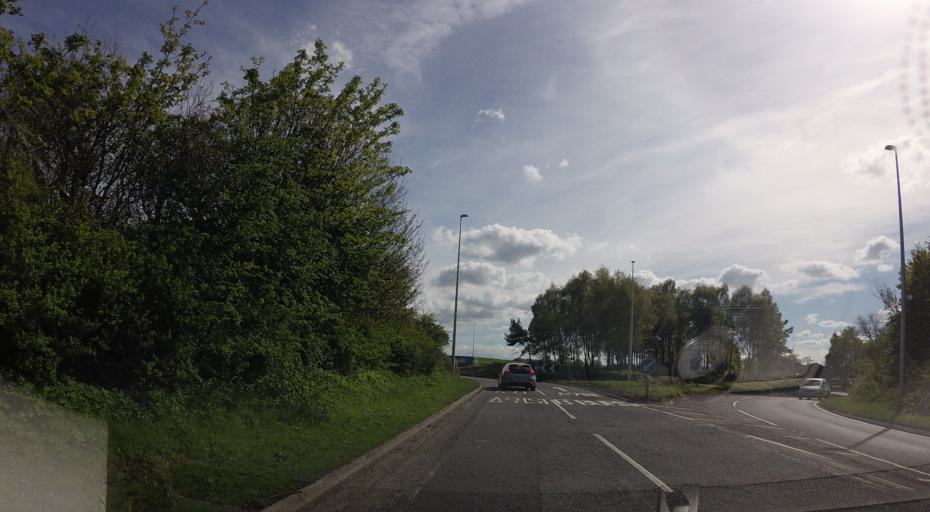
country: GB
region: Scotland
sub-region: Stirling
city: Bannockburn
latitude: 56.0862
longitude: -3.9041
